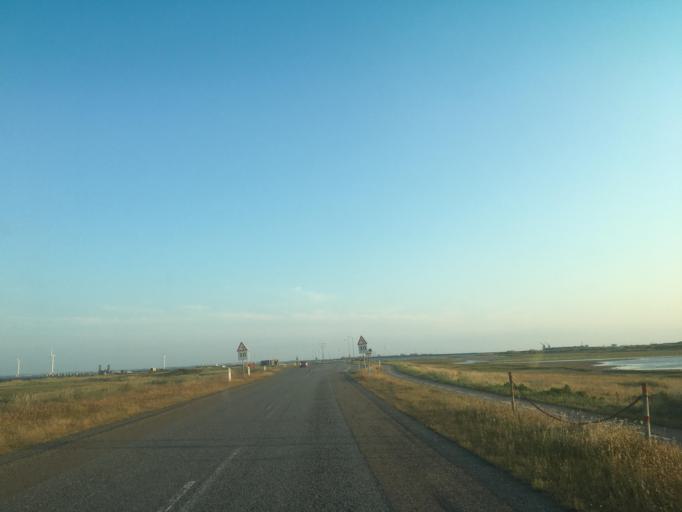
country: DK
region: Central Jutland
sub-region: Lemvig Kommune
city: Thyboron
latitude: 56.7062
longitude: 8.2472
